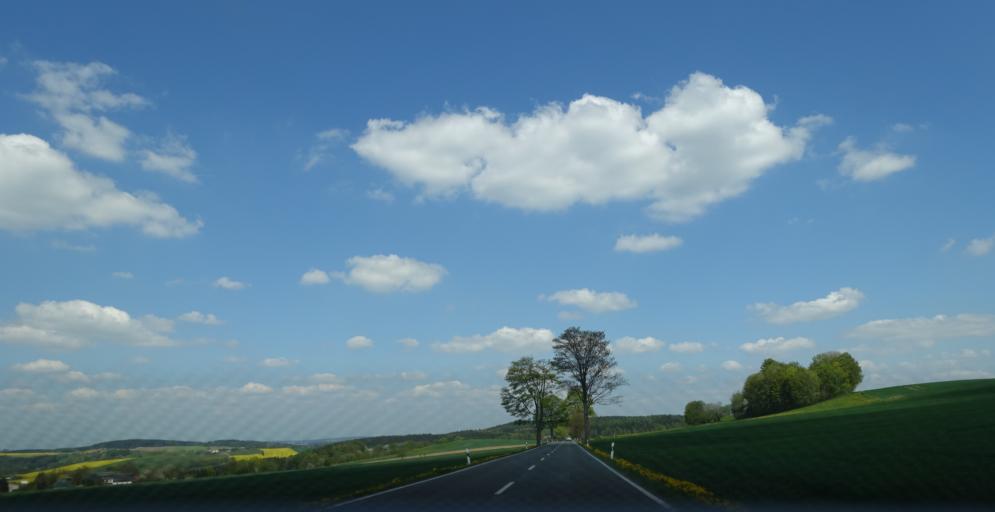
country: DE
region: Saxony
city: Grossolbersdorf
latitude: 50.7248
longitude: 13.1120
